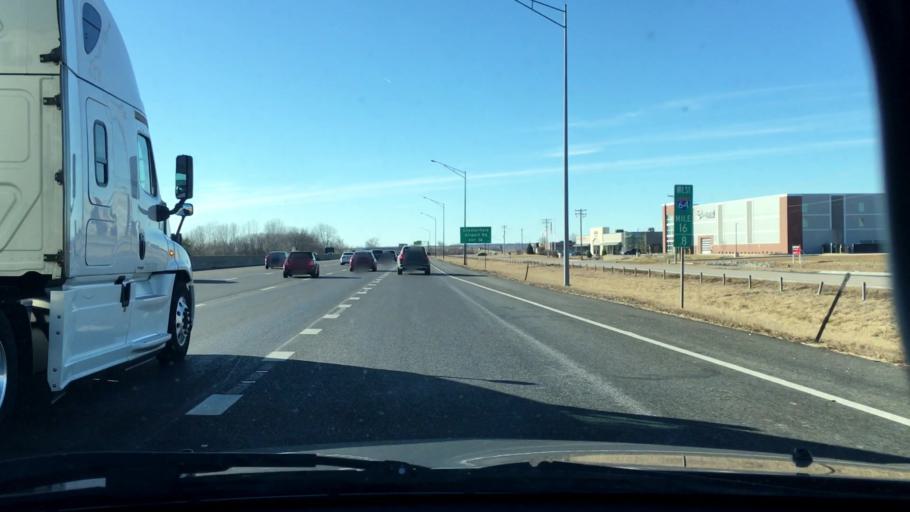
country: US
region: Missouri
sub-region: Saint Louis County
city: Chesterfield
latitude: 38.6712
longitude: -90.6057
